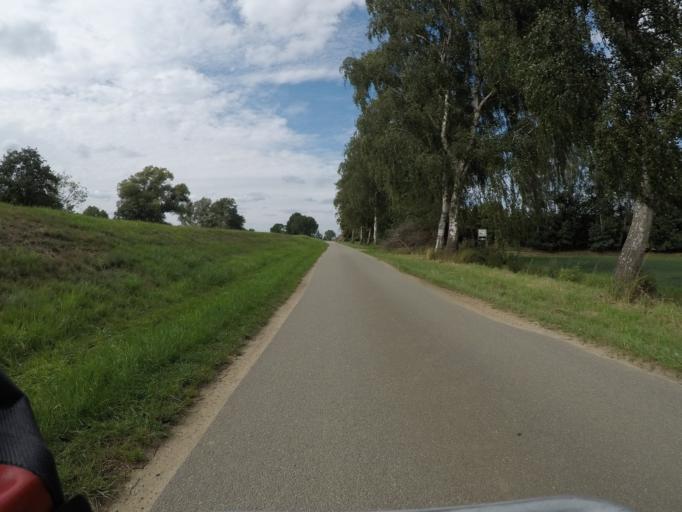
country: DE
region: Lower Saxony
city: Wittorf
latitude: 53.3457
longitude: 10.3843
